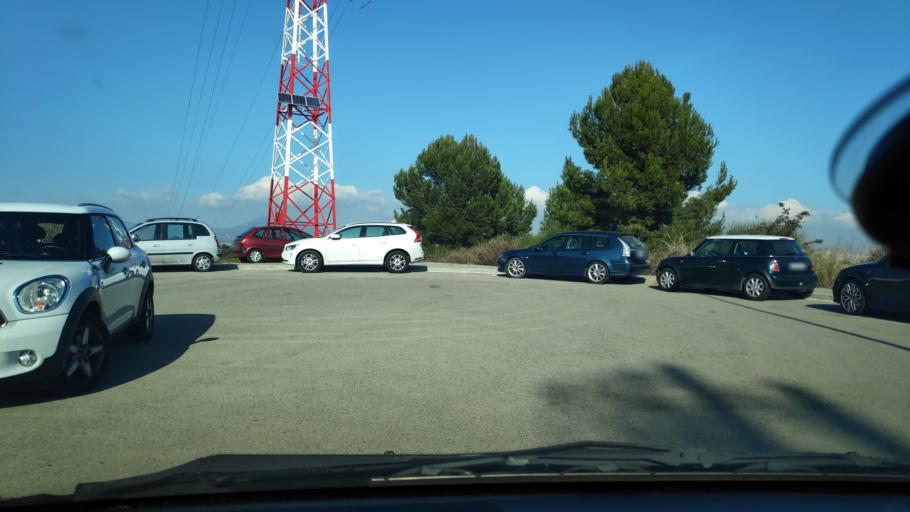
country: ES
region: Catalonia
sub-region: Provincia de Barcelona
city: Sant Quirze del Valles
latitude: 41.5155
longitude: 2.0957
